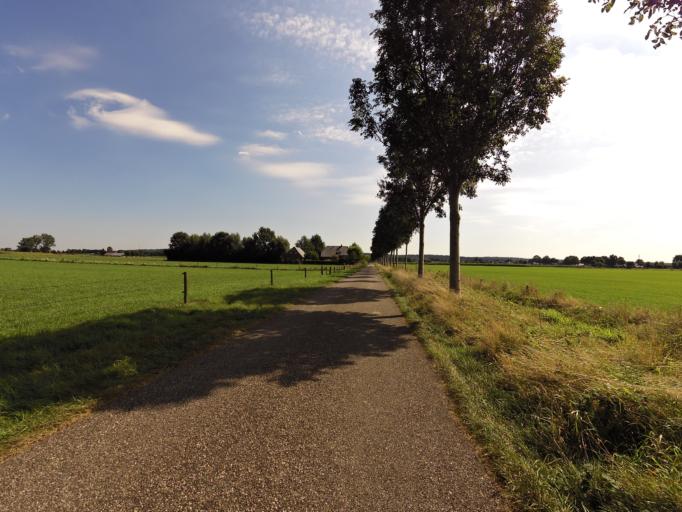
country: NL
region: Gelderland
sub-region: Gemeente Montferland
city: s-Heerenberg
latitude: 51.9300
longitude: 6.1856
